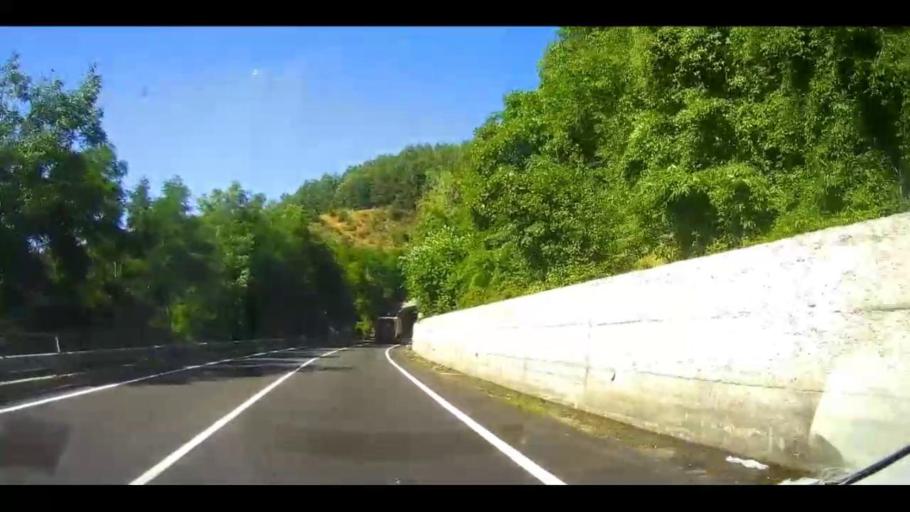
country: IT
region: Calabria
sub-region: Provincia di Cosenza
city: Celico
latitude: 39.3345
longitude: 16.3595
